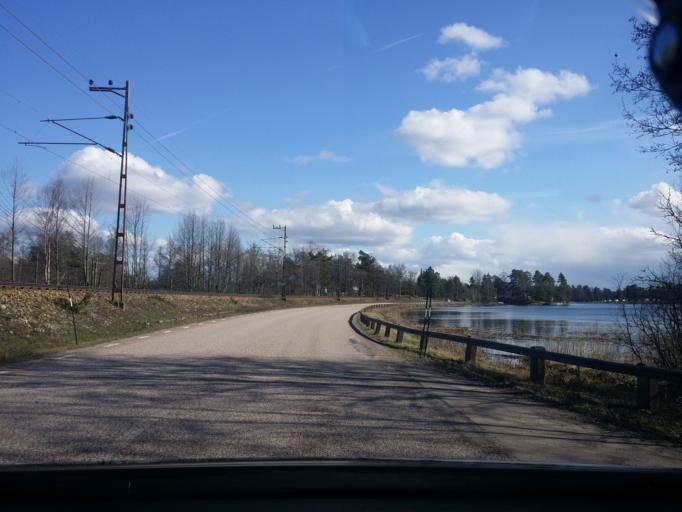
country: SE
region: Vaestmanland
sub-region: Sala Kommun
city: Sala
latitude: 59.9628
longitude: 16.5117
